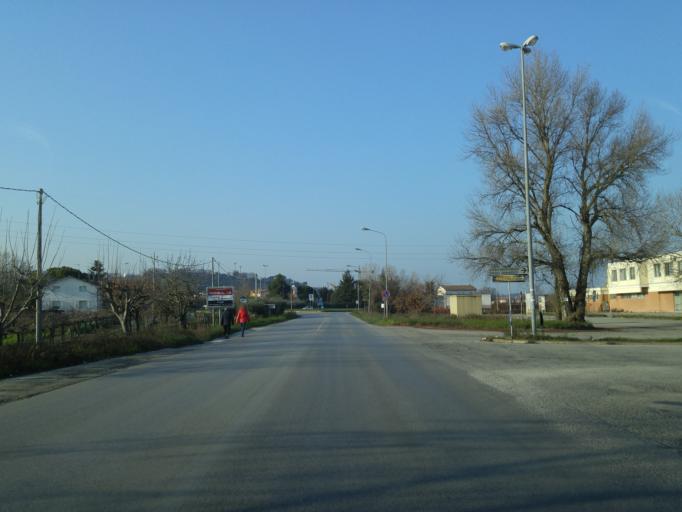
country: IT
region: The Marches
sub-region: Provincia di Pesaro e Urbino
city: Rosciano
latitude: 43.8147
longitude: 13.0005
